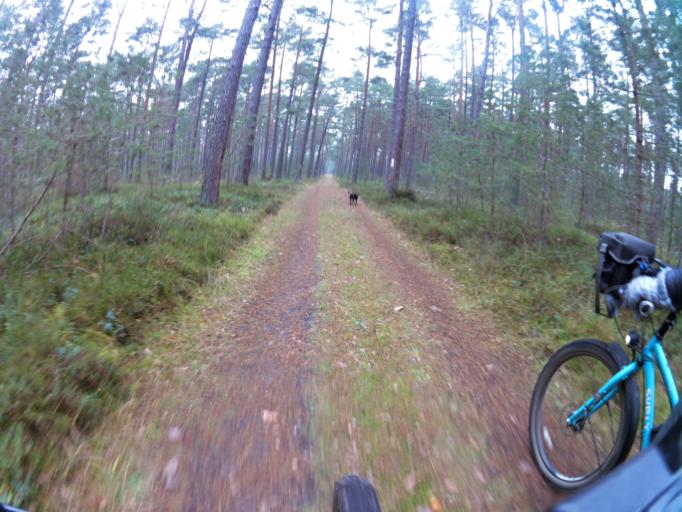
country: PL
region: West Pomeranian Voivodeship
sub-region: Powiat gryficki
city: Cerkwica
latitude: 54.1036
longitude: 15.1437
